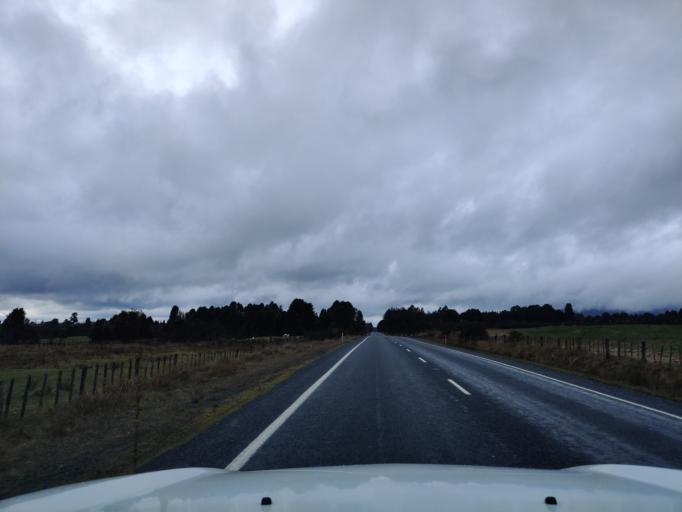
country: NZ
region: Manawatu-Wanganui
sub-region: Ruapehu District
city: Waiouru
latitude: -39.2947
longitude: 175.3877
